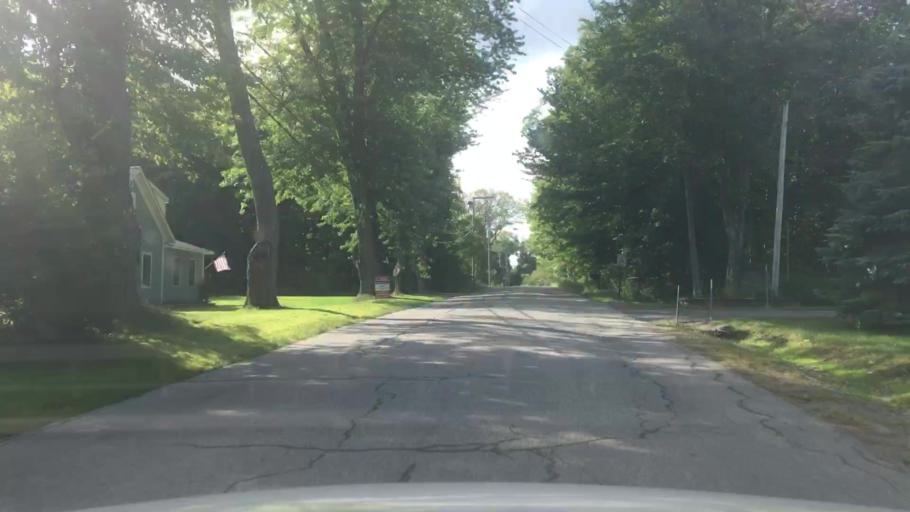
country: US
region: Maine
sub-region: Kennebec County
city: Gardiner
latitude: 44.1823
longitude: -69.8258
